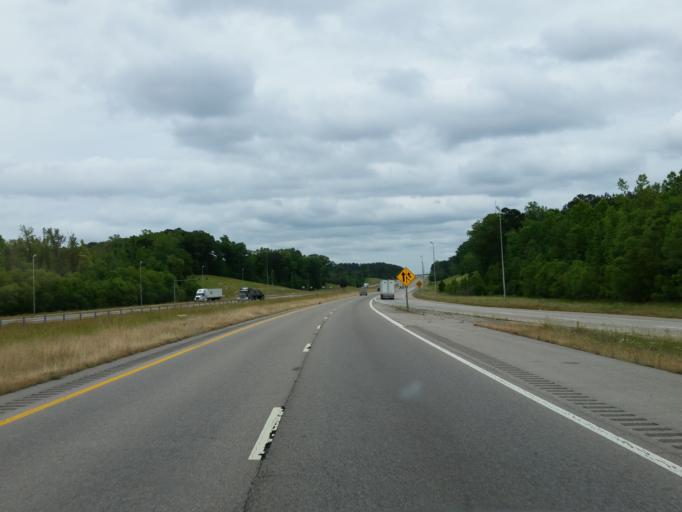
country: US
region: Alabama
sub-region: Sumter County
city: York
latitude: 32.4397
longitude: -88.4323
